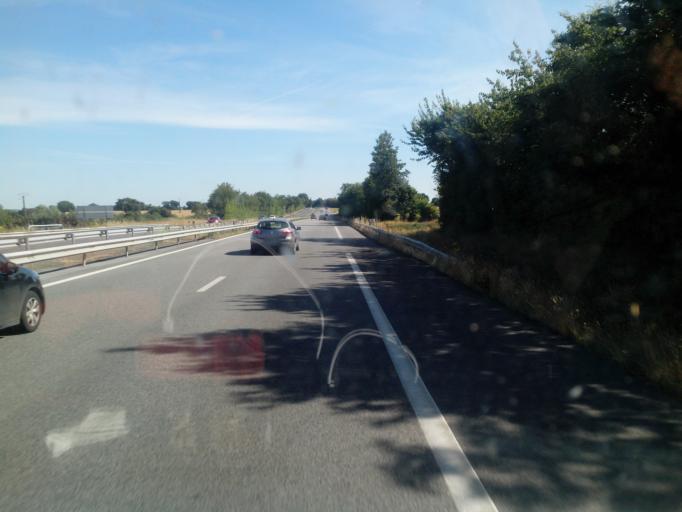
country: FR
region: Brittany
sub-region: Departement d'Ille-et-Vilaine
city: Grand-Fougeray
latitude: 47.7350
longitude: -1.7129
